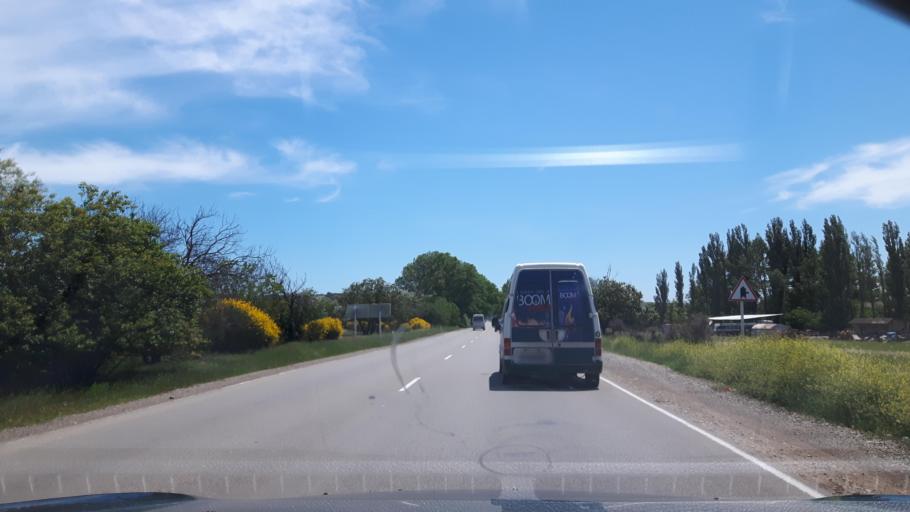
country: GE
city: Didi Lilo
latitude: 41.6953
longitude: 45.0567
